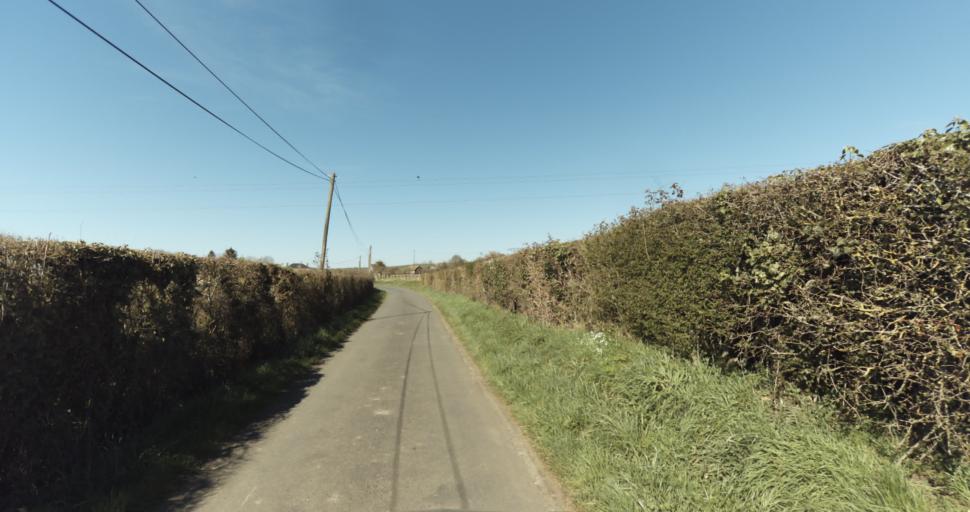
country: FR
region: Lower Normandy
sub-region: Departement du Calvados
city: Saint-Pierre-sur-Dives
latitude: 49.0633
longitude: -0.0288
